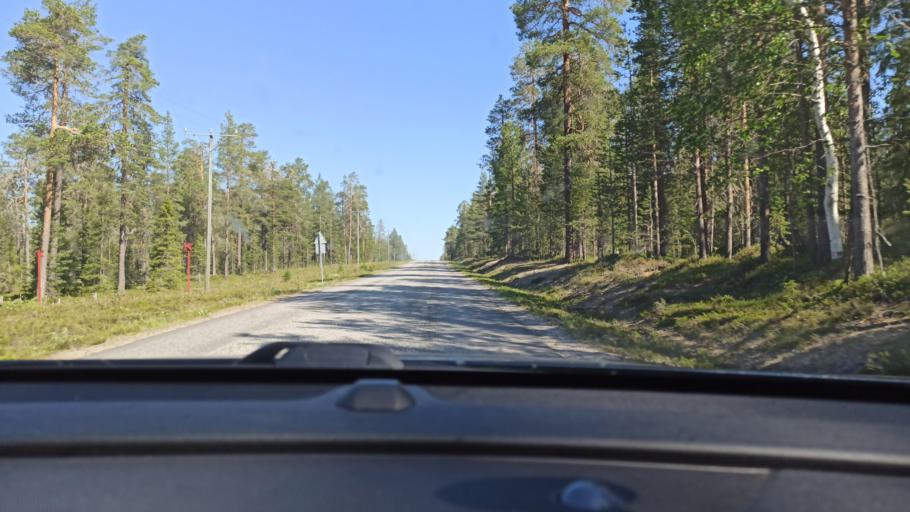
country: FI
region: Lapland
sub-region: Tunturi-Lappi
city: Kolari
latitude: 67.6388
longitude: 24.1569
